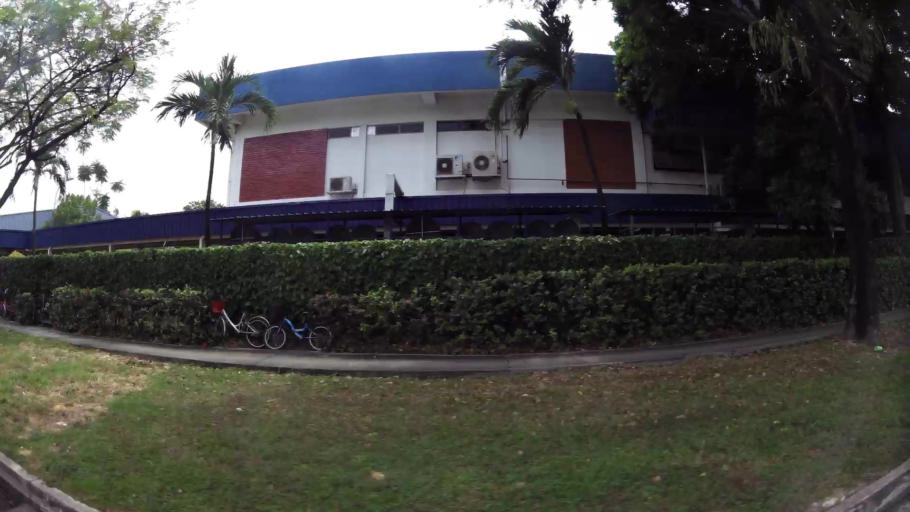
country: MY
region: Johor
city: Johor Bahru
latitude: 1.3225
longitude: 103.6904
